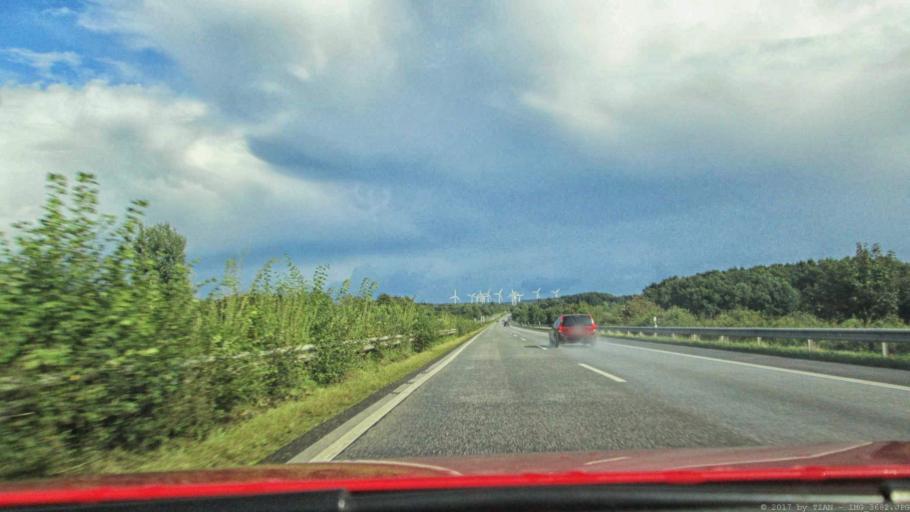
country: DE
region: Schleswig-Holstein
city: Holstenniendorf
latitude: 54.0668
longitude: 9.3314
